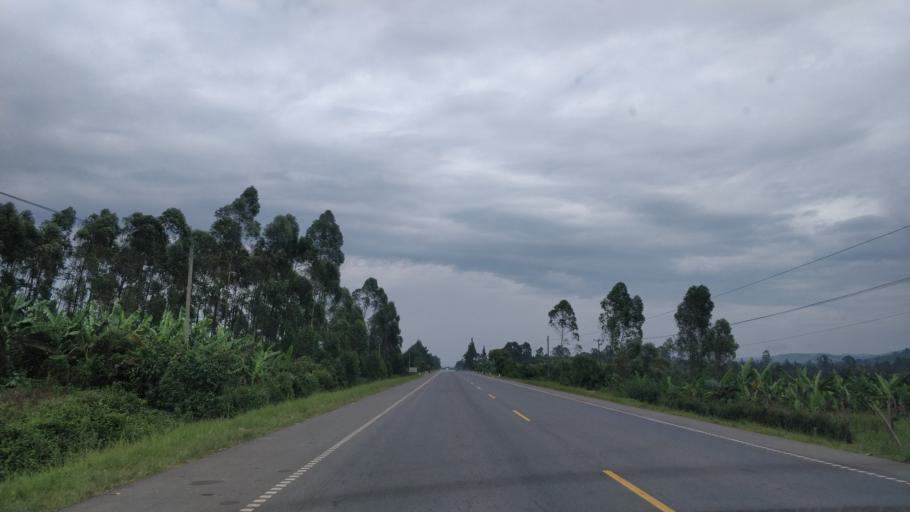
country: UG
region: Western Region
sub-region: Sheema District
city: Kibingo
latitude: -0.6736
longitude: 30.4254
